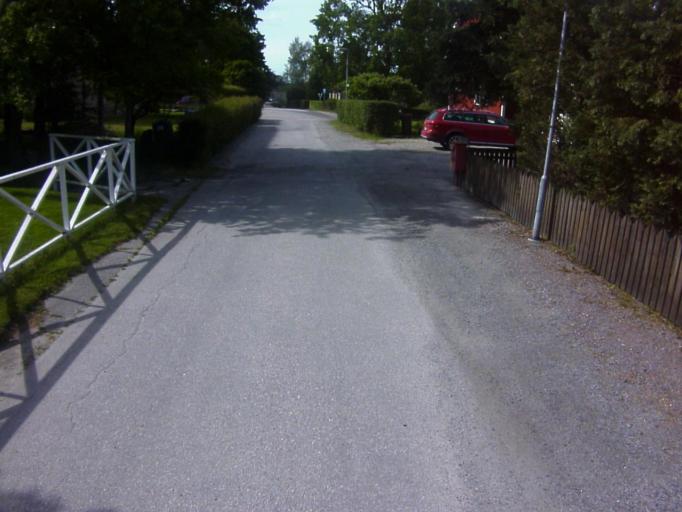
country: SE
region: Soedermanland
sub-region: Eskilstuna Kommun
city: Skogstorp
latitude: 59.3302
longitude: 16.4844
